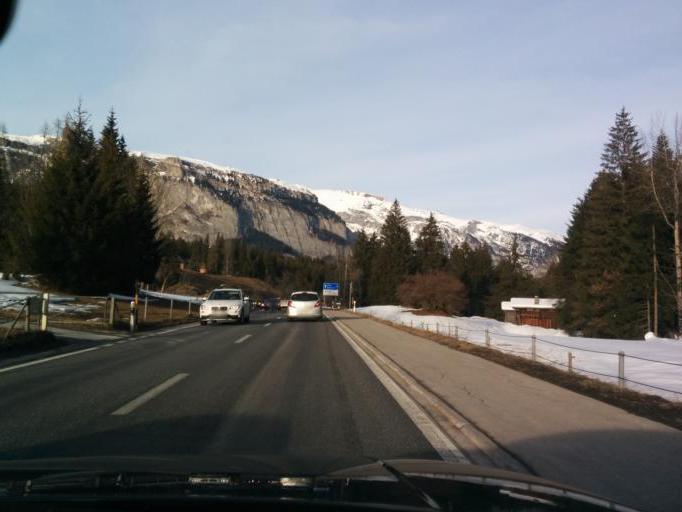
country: CH
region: Grisons
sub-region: Imboden District
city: Flims
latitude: 46.8218
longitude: 9.2704
